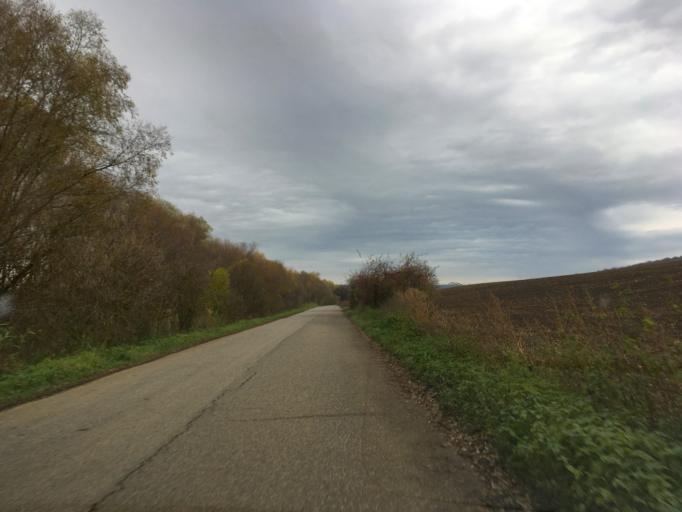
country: SK
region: Nitriansky
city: Svodin
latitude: 48.0439
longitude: 18.3708
